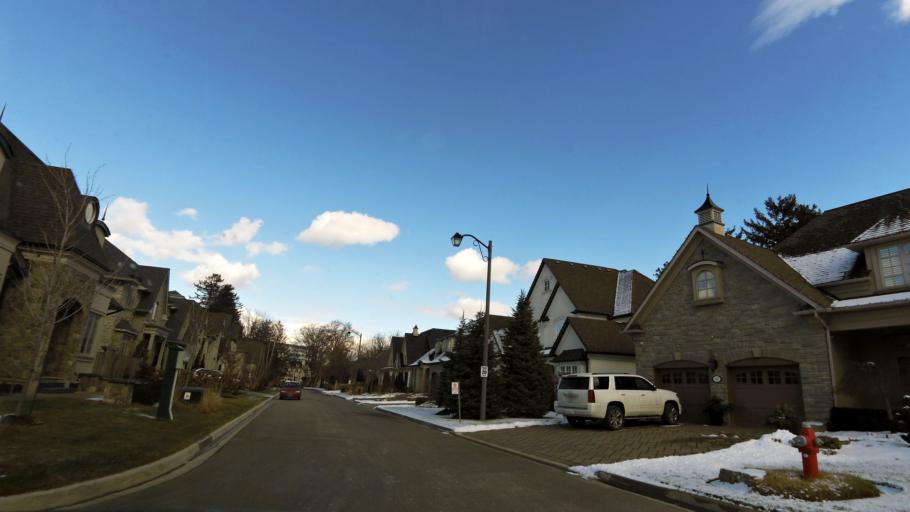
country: CA
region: Ontario
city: Mississauga
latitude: 43.5679
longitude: -79.6131
